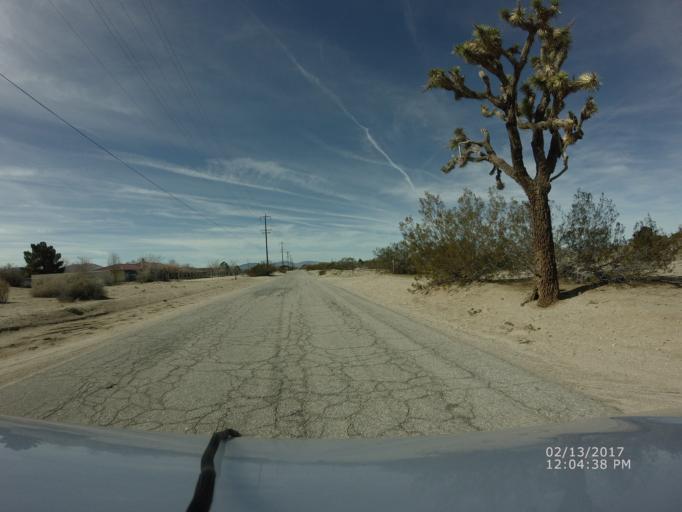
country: US
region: California
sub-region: Los Angeles County
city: Littlerock
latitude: 34.5580
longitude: -117.9294
